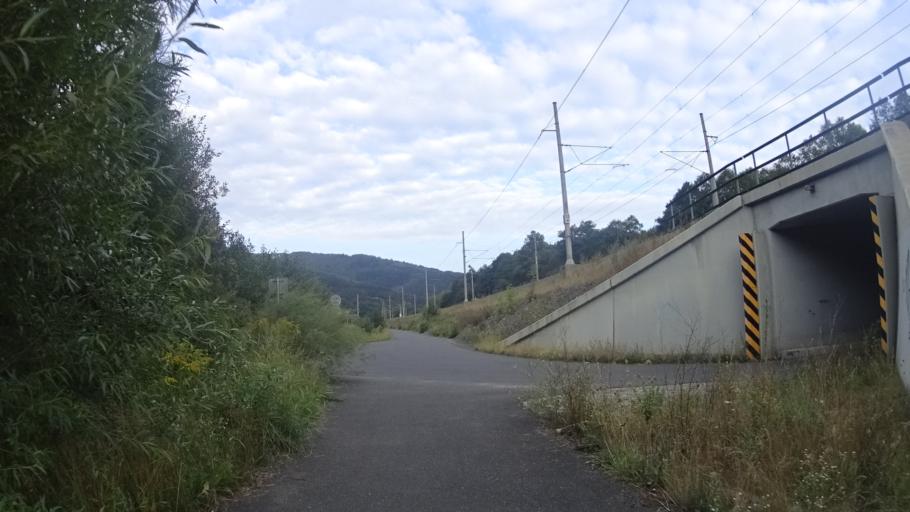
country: CZ
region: Olomoucky
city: Zabreh
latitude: 49.8657
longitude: 16.8047
